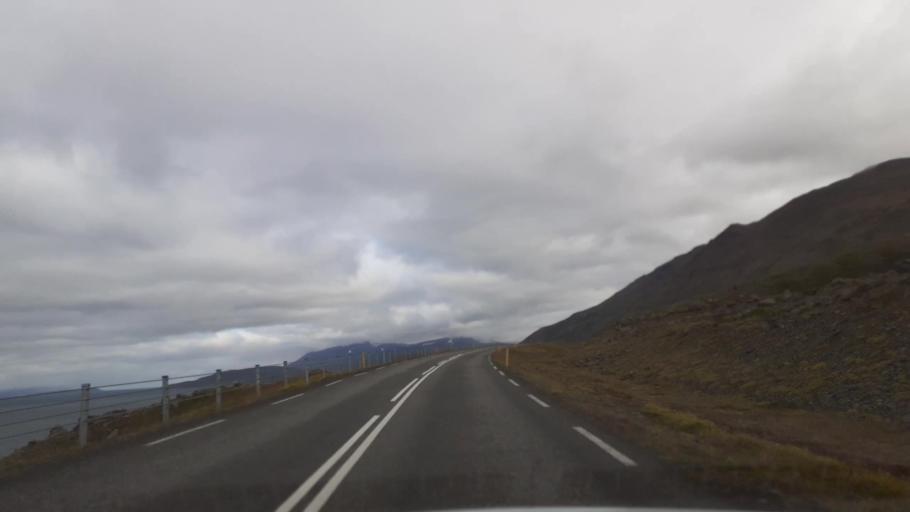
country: IS
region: Northeast
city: Akureyri
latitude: 65.8273
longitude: -18.0579
